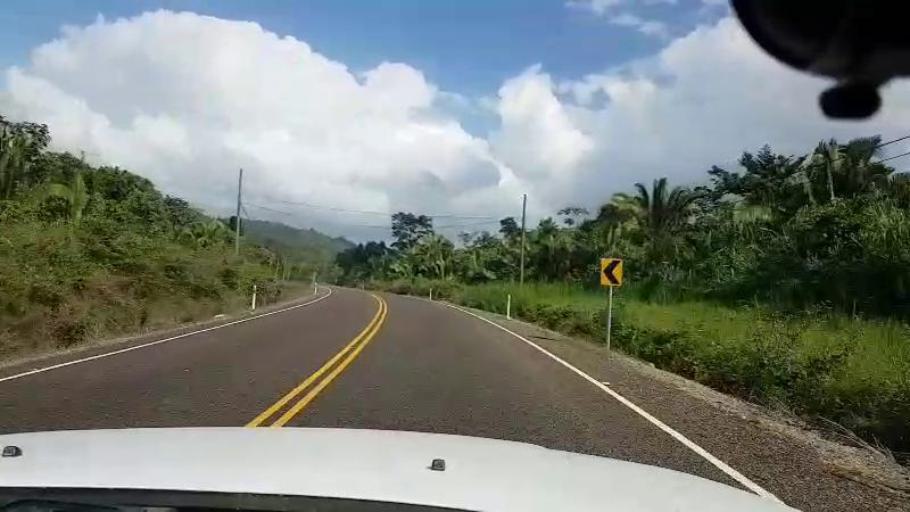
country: BZ
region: Cayo
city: Belmopan
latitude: 17.1458
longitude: -88.7292
